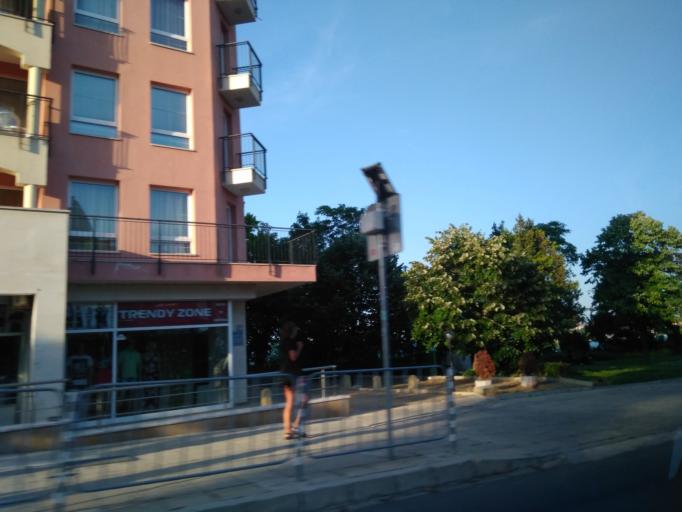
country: BG
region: Burgas
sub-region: Obshtina Nesebur
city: Nesebar
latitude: 42.6609
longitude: 27.7229
